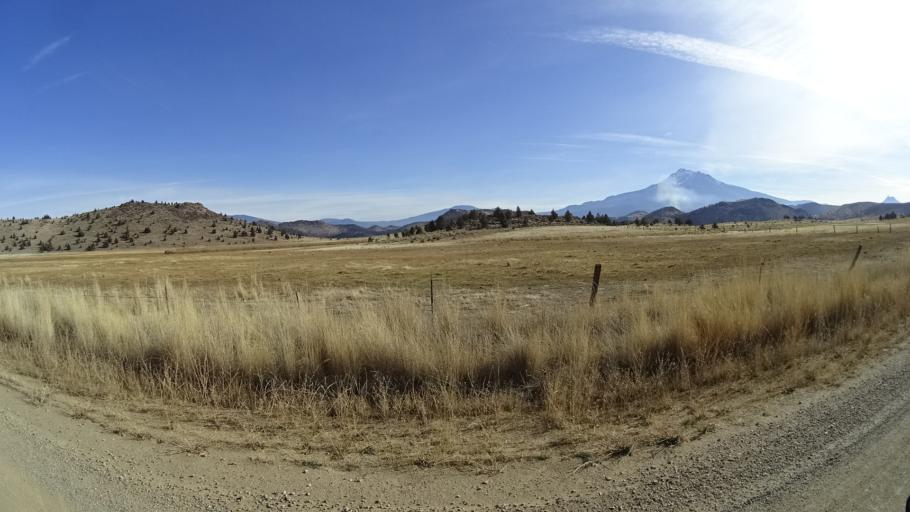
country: US
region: California
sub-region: Siskiyou County
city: Weed
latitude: 41.5420
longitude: -122.4726
